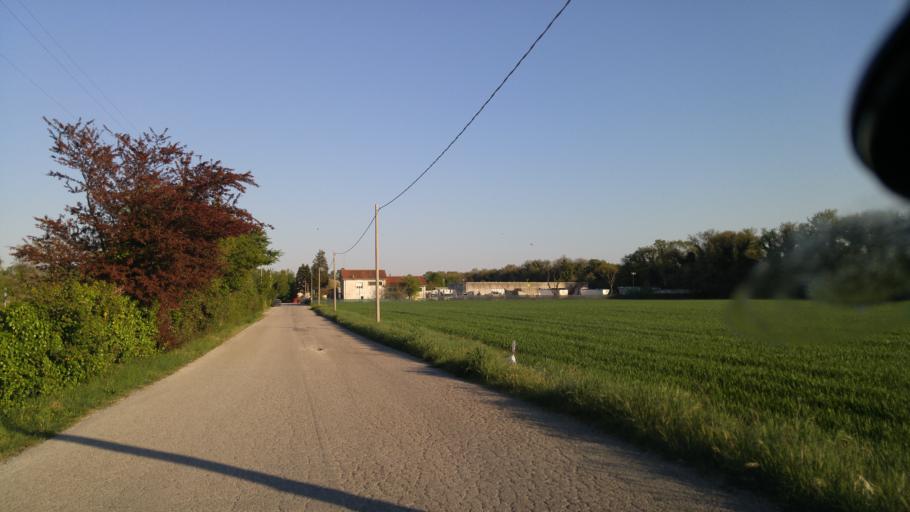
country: IT
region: The Marches
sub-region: Provincia di Pesaro e Urbino
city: Fano
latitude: 43.8202
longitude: 13.0371
